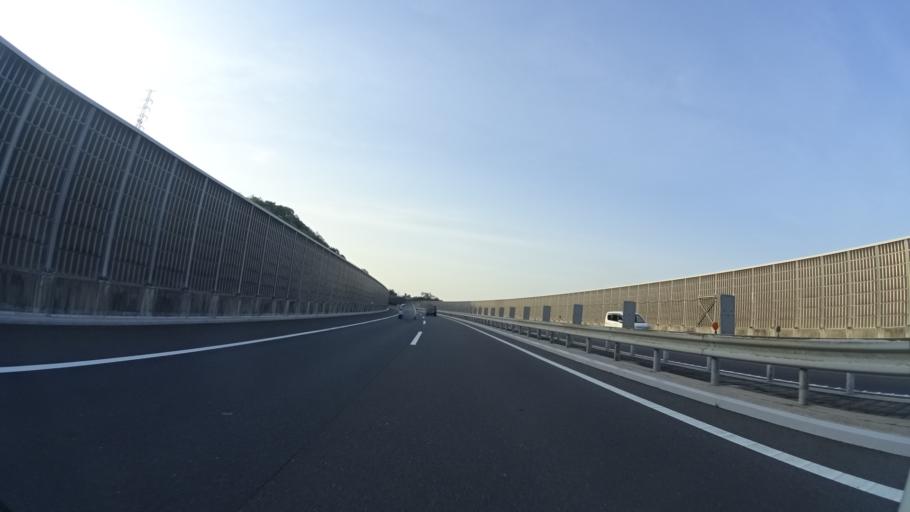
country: JP
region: Kagawa
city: Sakaidecho
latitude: 34.3132
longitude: 133.8393
